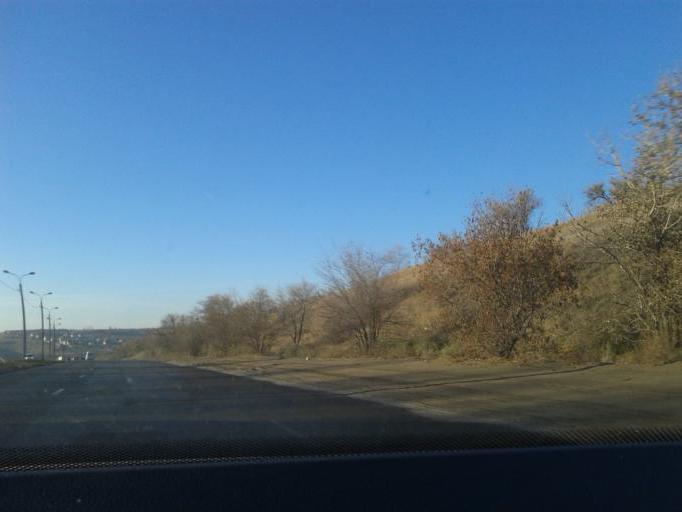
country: RU
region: Volgograd
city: Volgograd
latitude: 48.7265
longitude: 44.4476
